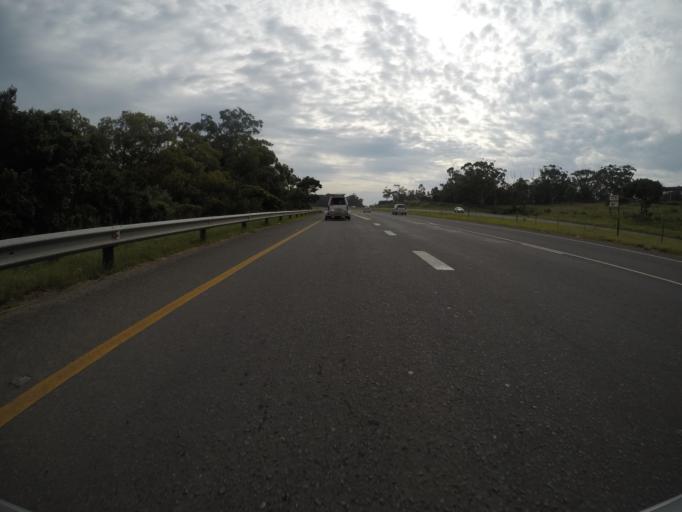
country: ZA
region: Eastern Cape
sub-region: Buffalo City Metropolitan Municipality
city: East London
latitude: -32.9403
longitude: 27.9470
